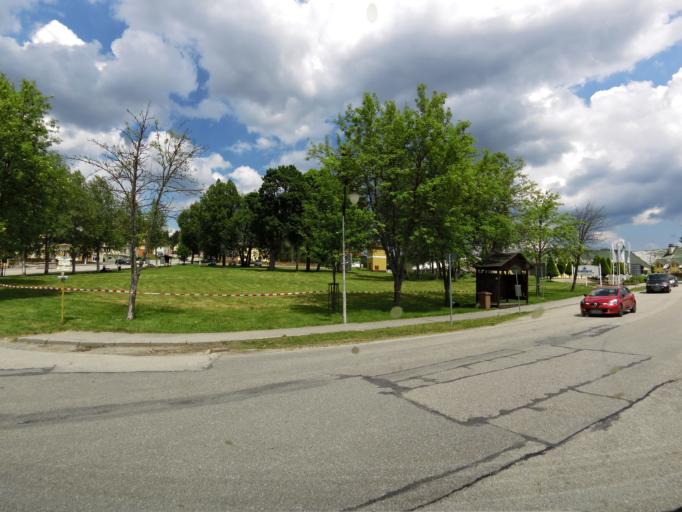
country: DE
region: Bavaria
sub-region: Lower Bavaria
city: Philippsreut
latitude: 48.9069
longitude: 13.7212
